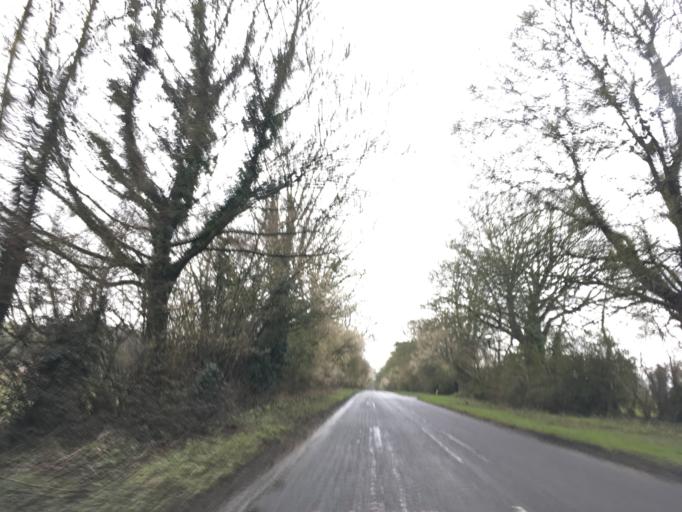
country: GB
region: England
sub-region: Borough of Swindon
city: Wanborough
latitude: 51.5337
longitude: -1.6730
